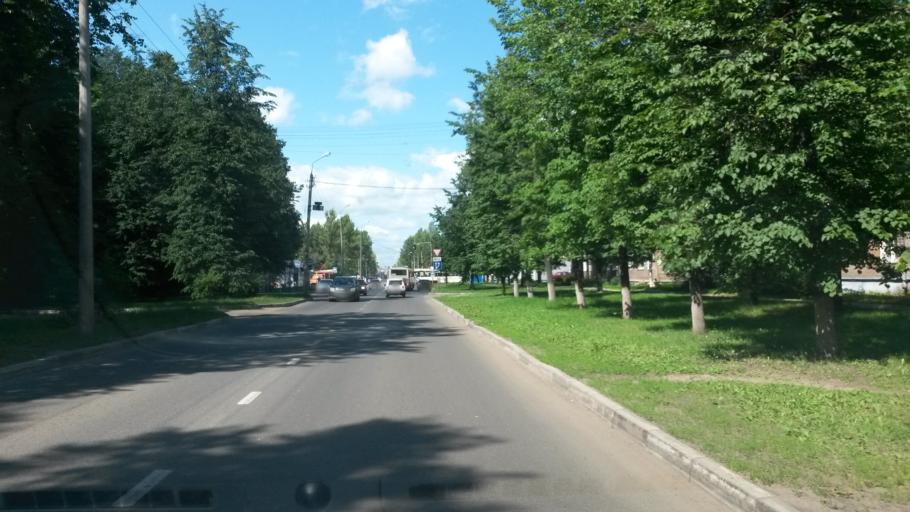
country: RU
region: Jaroslavl
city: Yaroslavl
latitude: 57.6359
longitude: 39.8231
